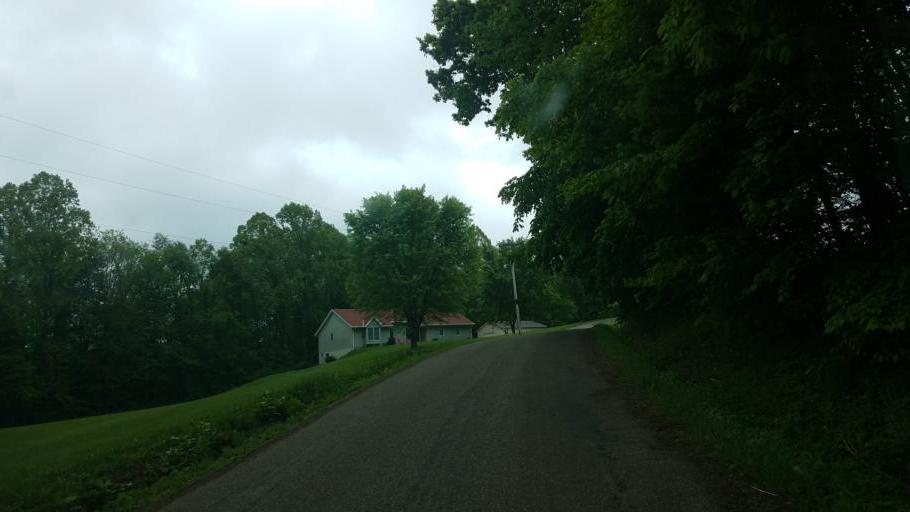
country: US
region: Ohio
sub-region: Richland County
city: Lincoln Heights
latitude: 40.7488
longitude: -82.3827
